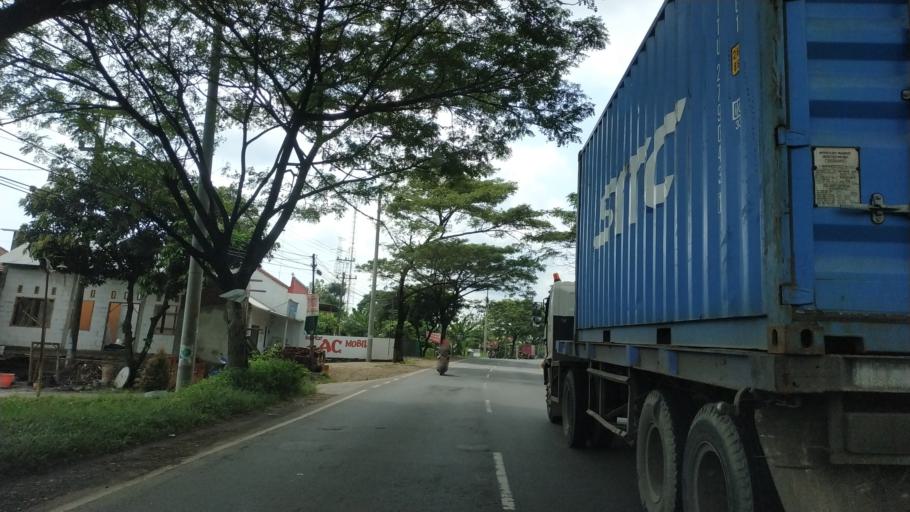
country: ID
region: Central Java
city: Pekalongan
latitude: -6.9507
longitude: 109.7957
